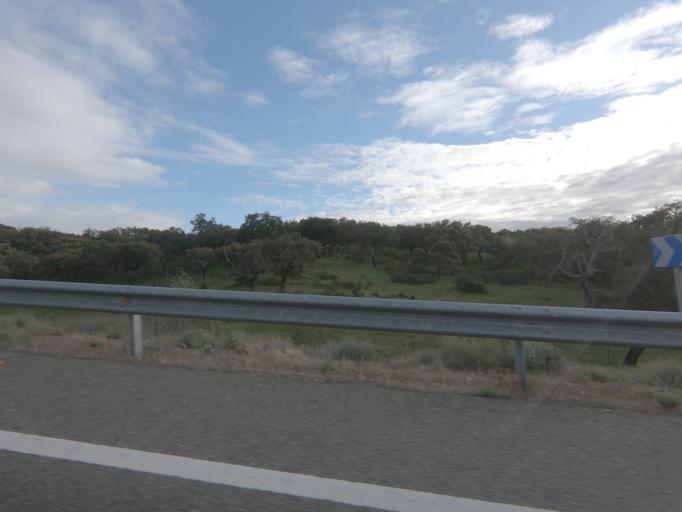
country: ES
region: Extremadura
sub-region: Provincia de Caceres
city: Pedroso de Acim
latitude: 39.8277
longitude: -6.3787
